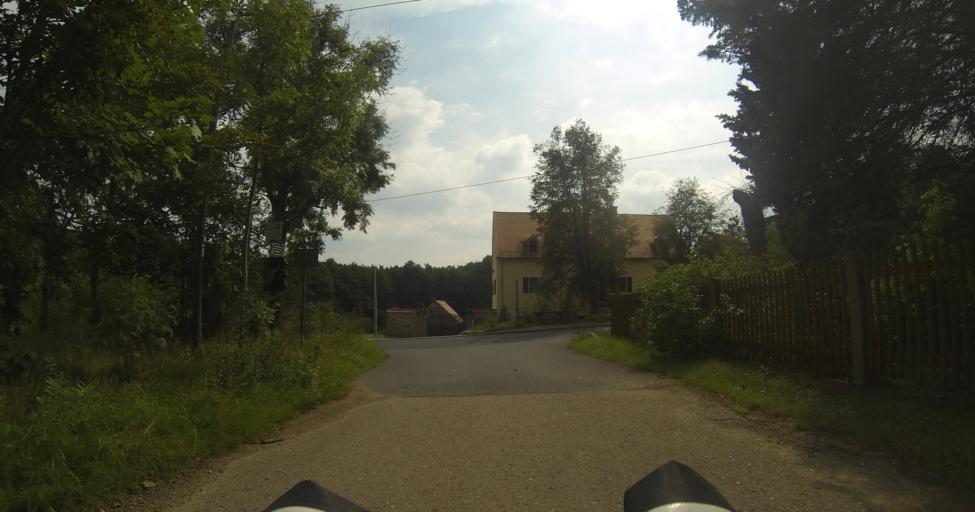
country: DE
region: Saxony
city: Coswig
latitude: 51.1569
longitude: 13.6217
